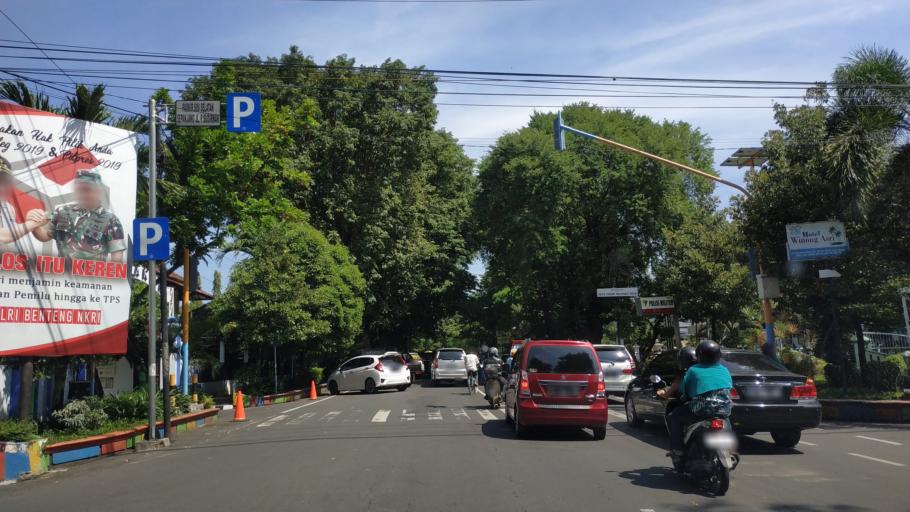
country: ID
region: Central Java
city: Pati
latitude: -6.7515
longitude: 111.0330
